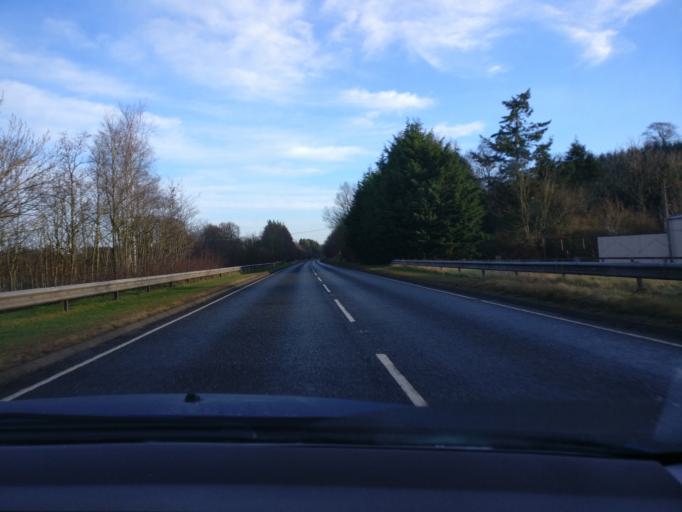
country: GB
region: Scotland
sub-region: The Scottish Borders
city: Hawick
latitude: 55.4508
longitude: -2.7199
